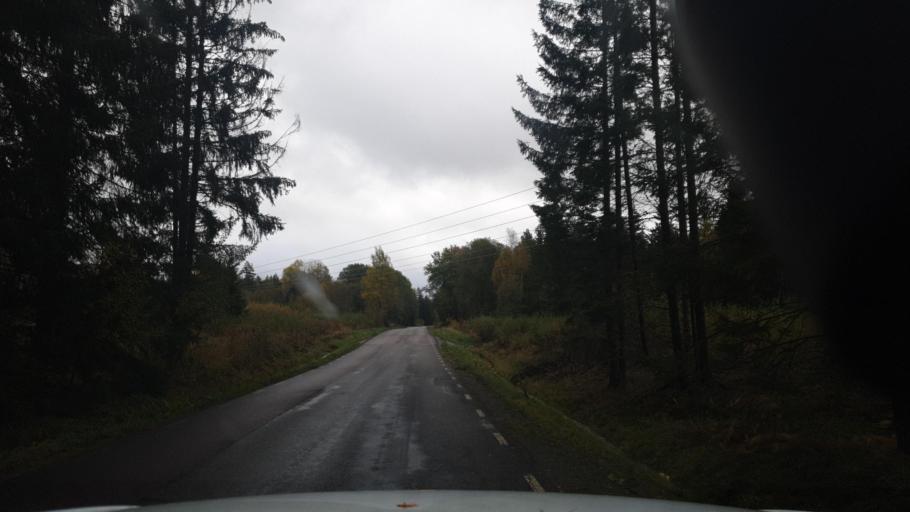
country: SE
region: Vaermland
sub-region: Karlstads Kommun
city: Valberg
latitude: 59.4137
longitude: 13.1632
